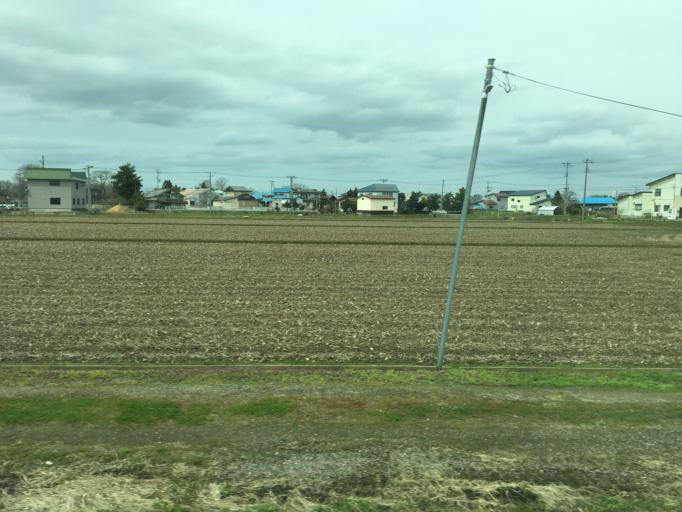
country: JP
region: Aomori
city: Shimokizukuri
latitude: 40.7868
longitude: 140.3634
